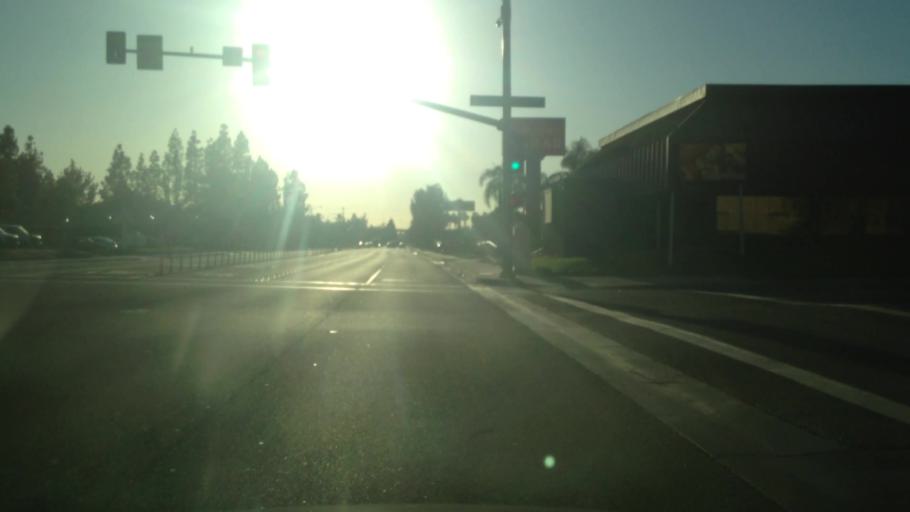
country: US
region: California
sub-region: San Bernardino County
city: Loma Linda
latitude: 34.0659
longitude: -117.2821
